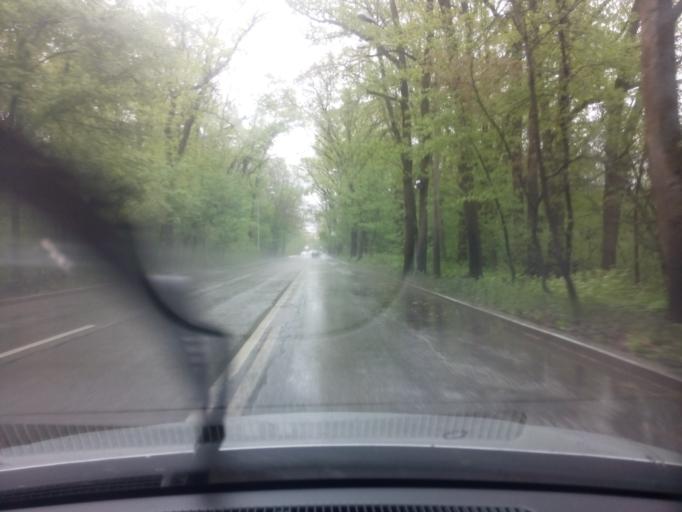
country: RO
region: Ilfov
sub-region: Comuna Otopeni
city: Otopeni
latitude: 44.5158
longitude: 26.0978
